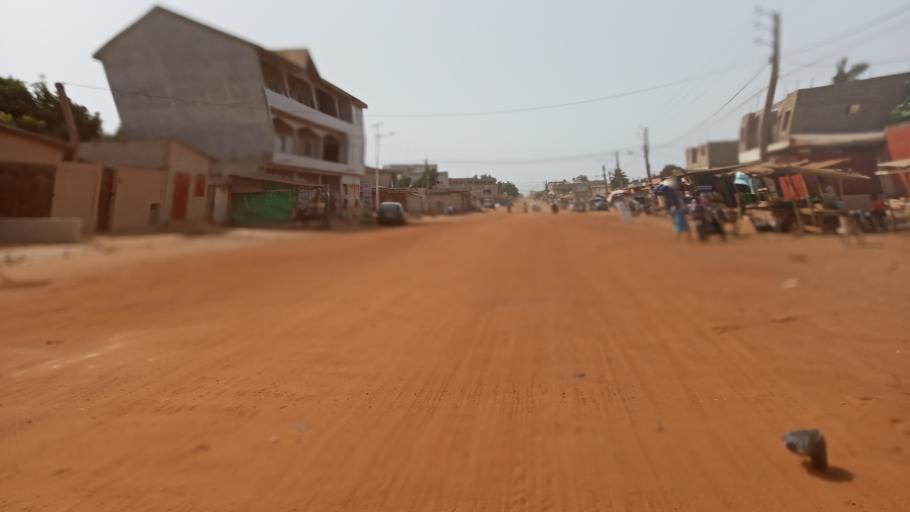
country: TG
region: Maritime
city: Lome
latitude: 6.2028
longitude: 1.1669
